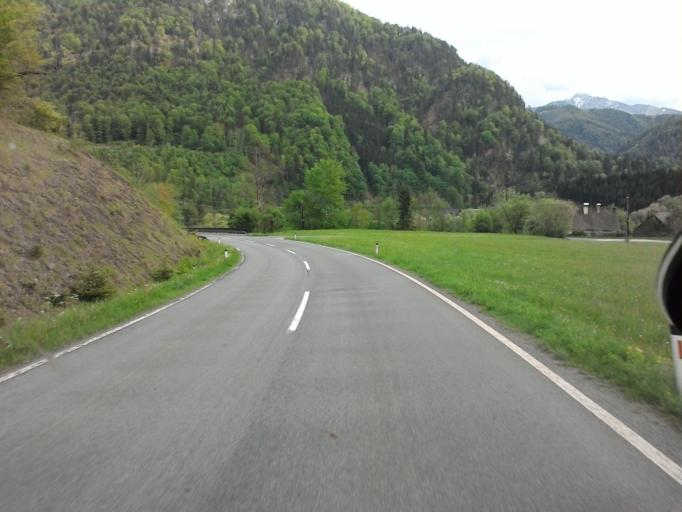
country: AT
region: Styria
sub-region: Politischer Bezirk Liezen
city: Altenmarkt bei Sankt Gallen
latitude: 47.7080
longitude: 14.6851
